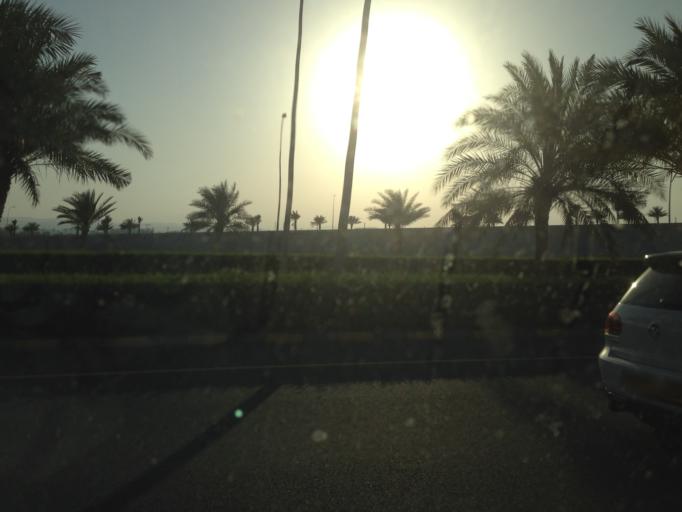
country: OM
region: Muhafazat Masqat
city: Bawshar
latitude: 23.5964
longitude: 58.3309
